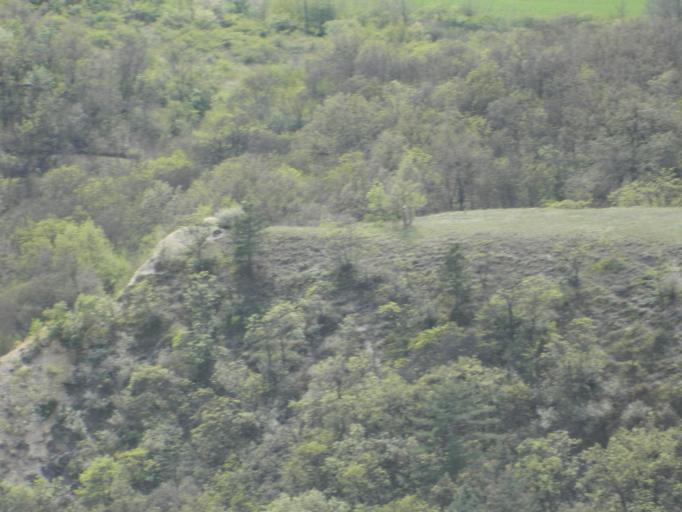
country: HU
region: Veszprem
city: Varpalota
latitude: 47.2208
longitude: 18.2013
